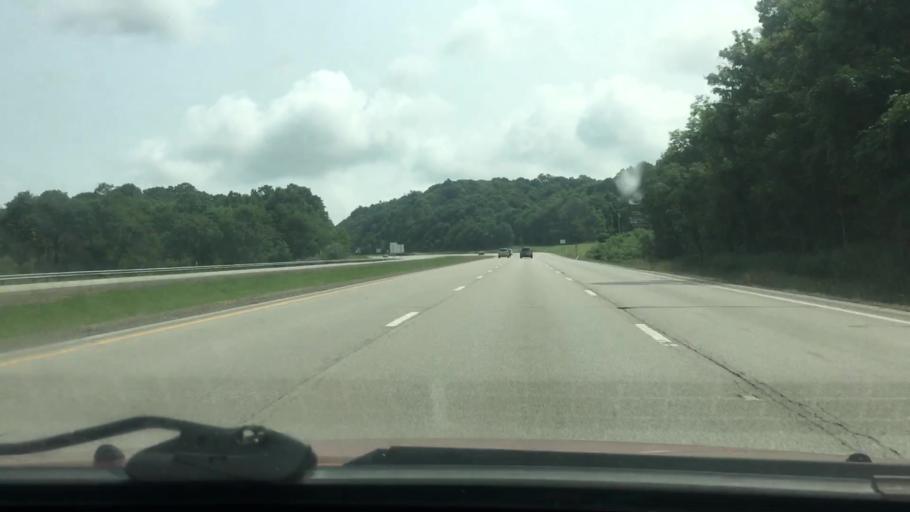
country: US
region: West Virginia
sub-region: Preston County
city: Terra Alta
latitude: 39.6575
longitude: -79.5148
